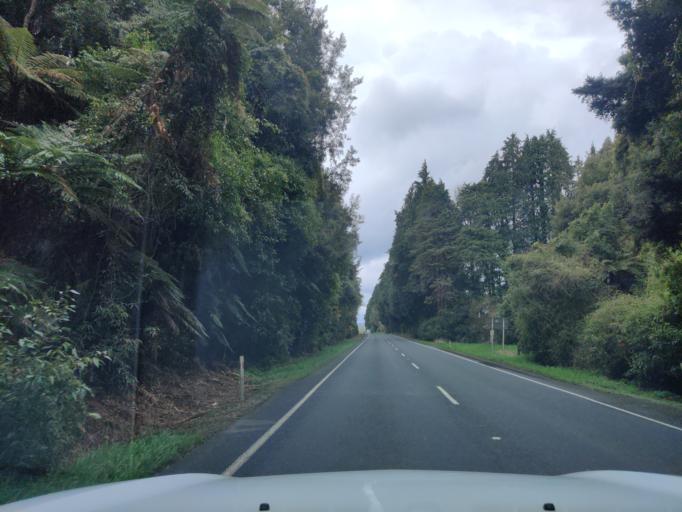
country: NZ
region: Waikato
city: Turangi
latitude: -38.9946
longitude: 175.3784
